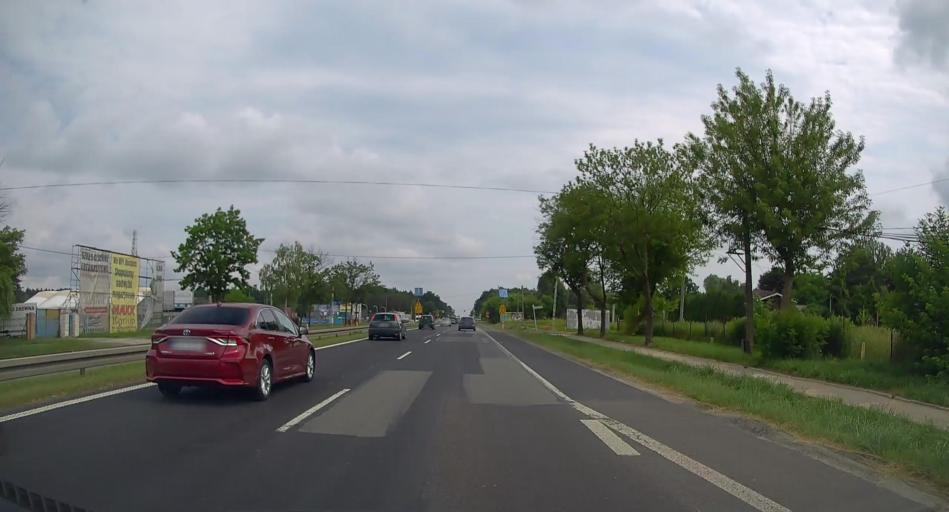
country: PL
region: Masovian Voivodeship
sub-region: Powiat piaseczynski
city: Lesznowola
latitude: 52.0893
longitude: 20.8812
